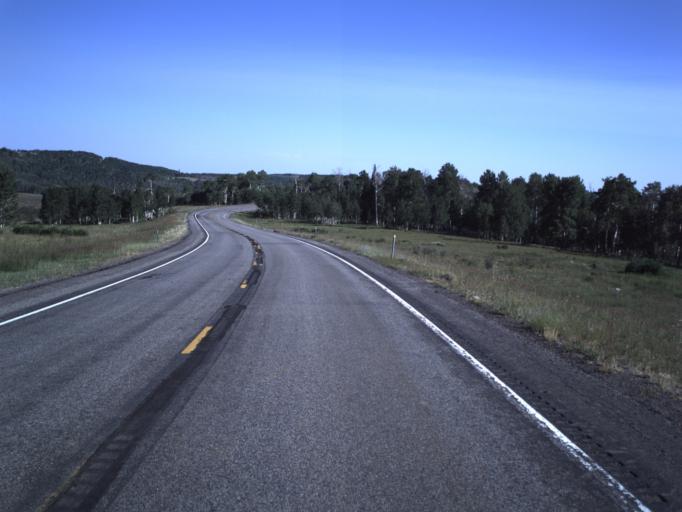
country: US
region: Utah
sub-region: Sanpete County
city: Fairview
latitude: 39.6511
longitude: -111.3289
